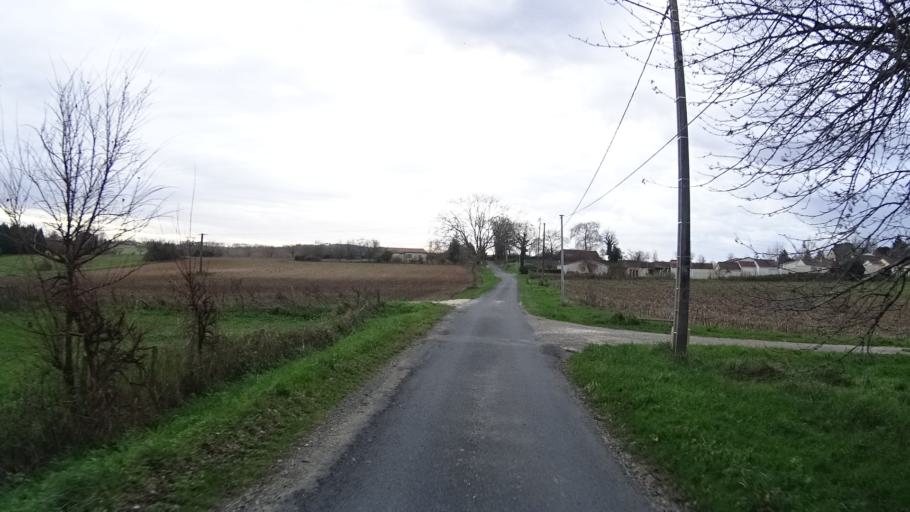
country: FR
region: Aquitaine
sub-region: Departement de la Dordogne
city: Saint-Aulaye
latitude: 45.2038
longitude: 0.1406
